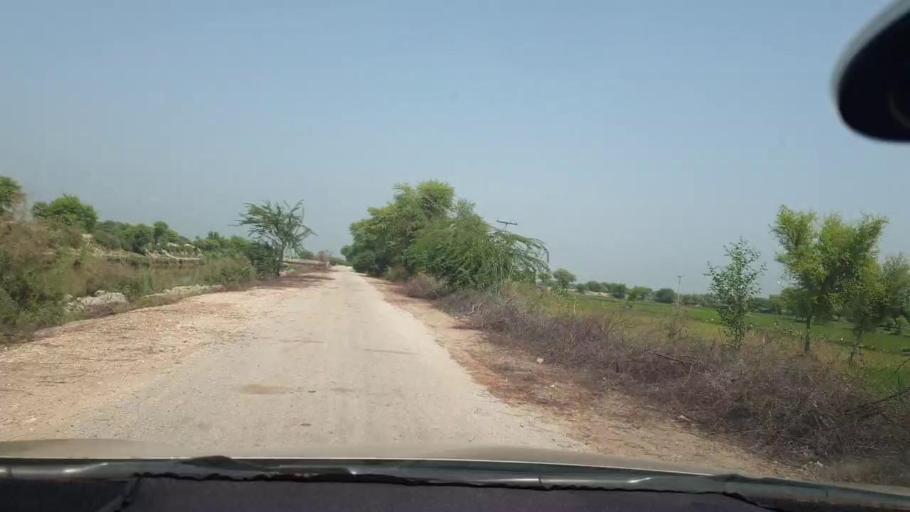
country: PK
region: Sindh
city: Kambar
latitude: 27.6693
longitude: 67.8956
